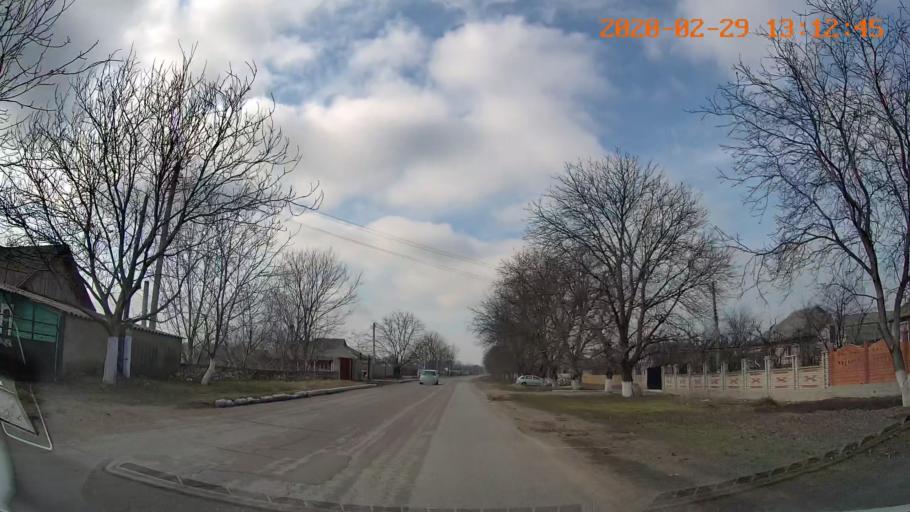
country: MD
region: Telenesti
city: Camenca
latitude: 48.0133
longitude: 28.6922
